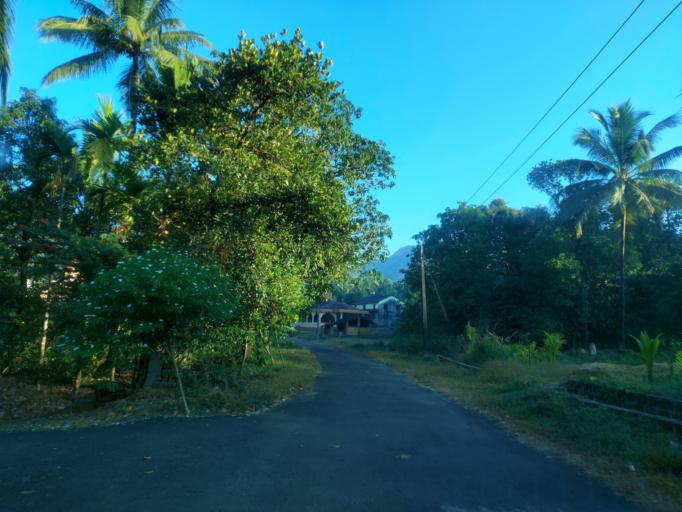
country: IN
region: Maharashtra
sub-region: Sindhudurg
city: Kudal
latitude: 16.0679
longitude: 73.8239
